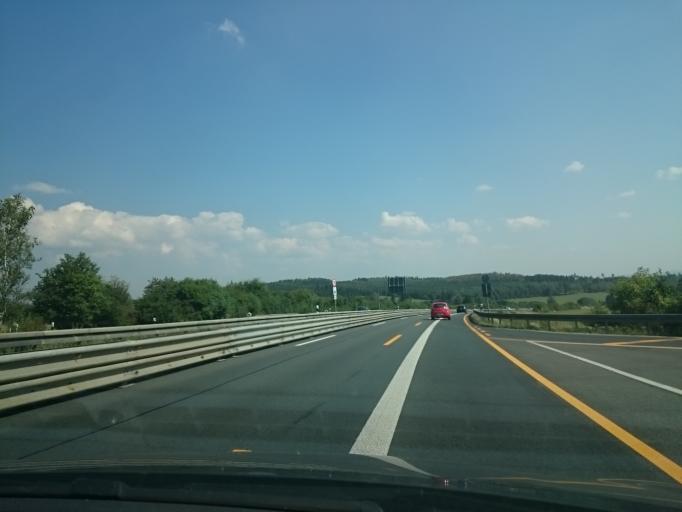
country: DE
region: Bavaria
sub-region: Upper Franconia
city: Trogen
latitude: 50.3947
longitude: 11.9921
